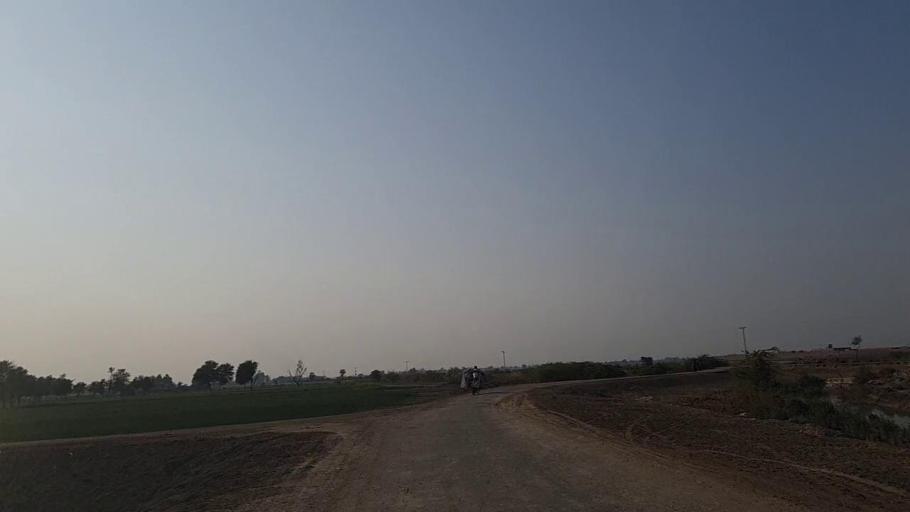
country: PK
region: Sindh
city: Jam Sahib
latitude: 26.2857
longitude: 68.6112
